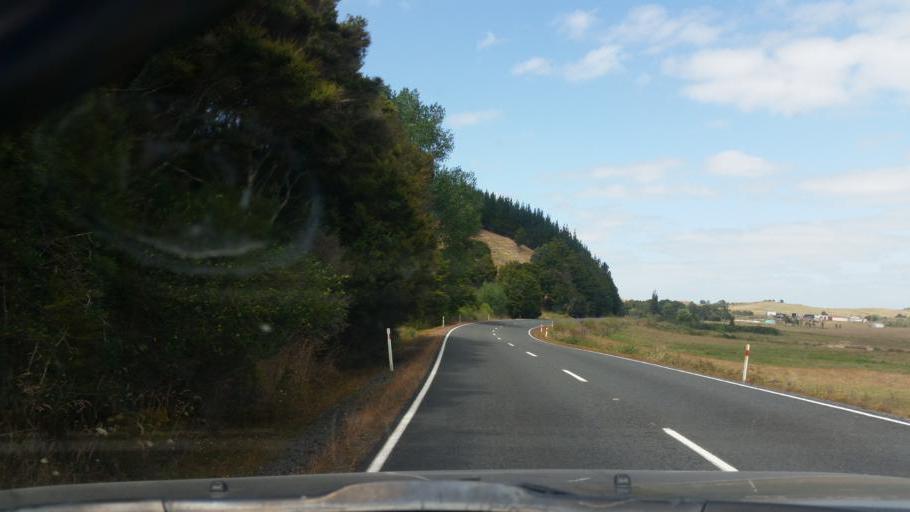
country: NZ
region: Northland
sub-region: Whangarei
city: Ruakaka
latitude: -35.9682
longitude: 174.2903
